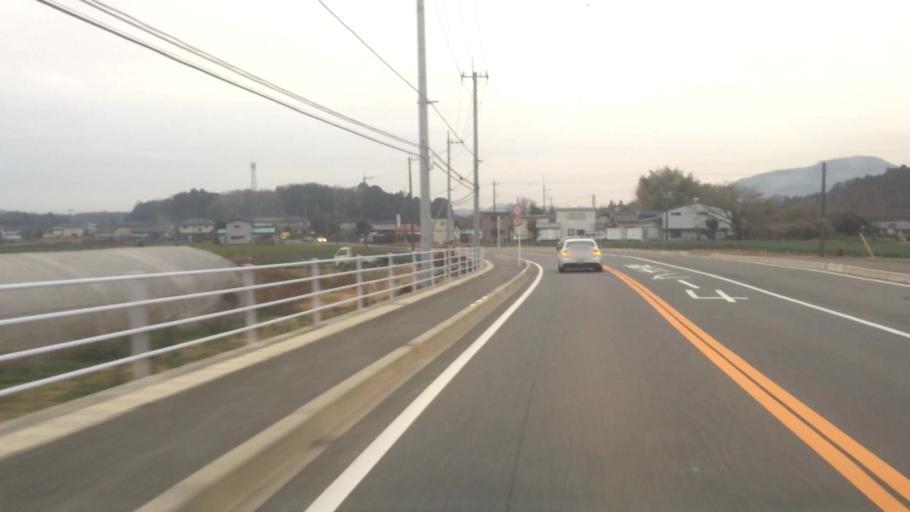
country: JP
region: Tochigi
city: Utsunomiya-shi
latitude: 36.6389
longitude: 139.8185
